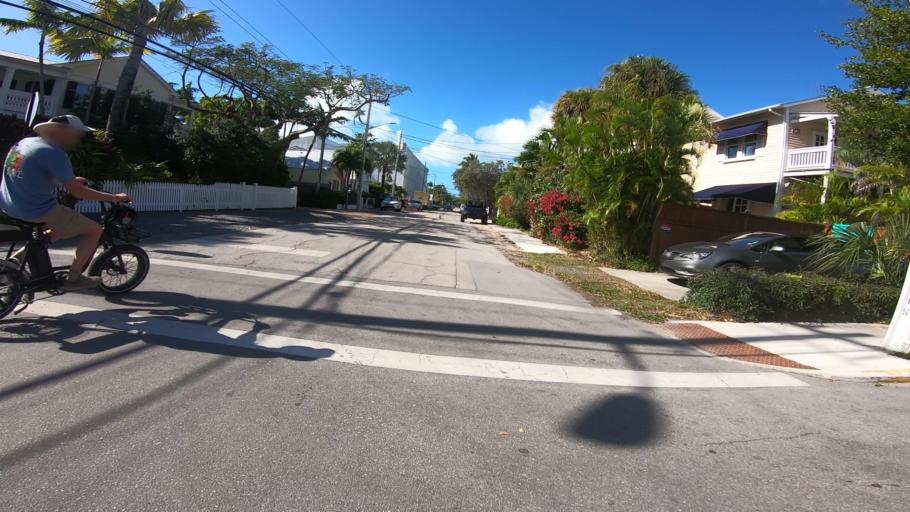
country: US
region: Florida
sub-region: Monroe County
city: Key West
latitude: 24.5521
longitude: -81.7911
